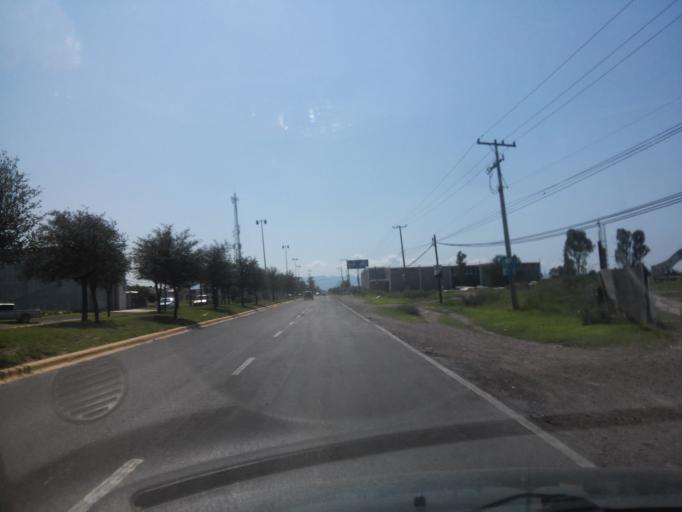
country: MX
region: Durango
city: Victoria de Durango
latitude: 23.9955
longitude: -104.6361
